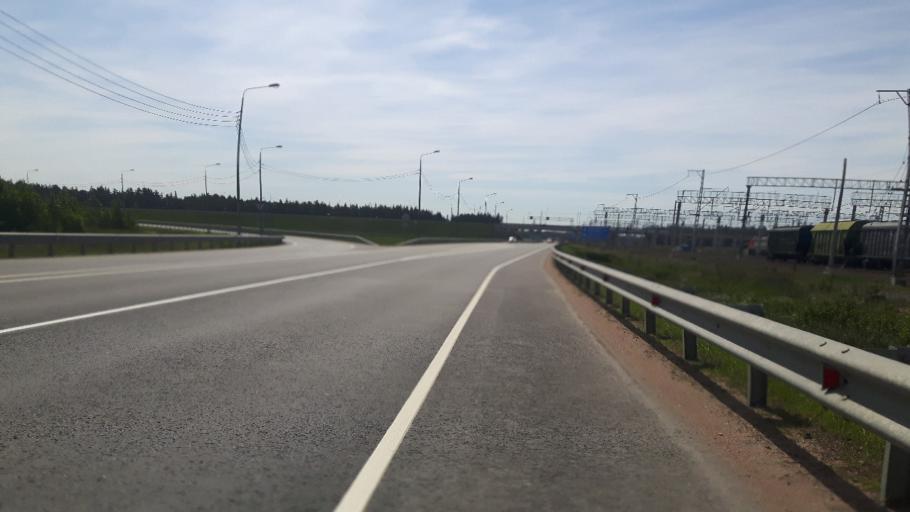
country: RU
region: Leningrad
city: Vistino
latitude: 59.6656
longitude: 28.4339
